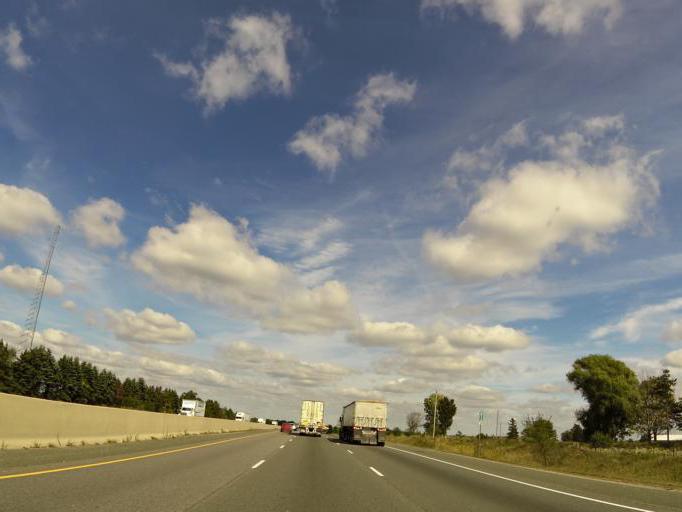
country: CA
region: Ontario
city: Ingersoll
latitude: 42.9838
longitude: -80.9160
